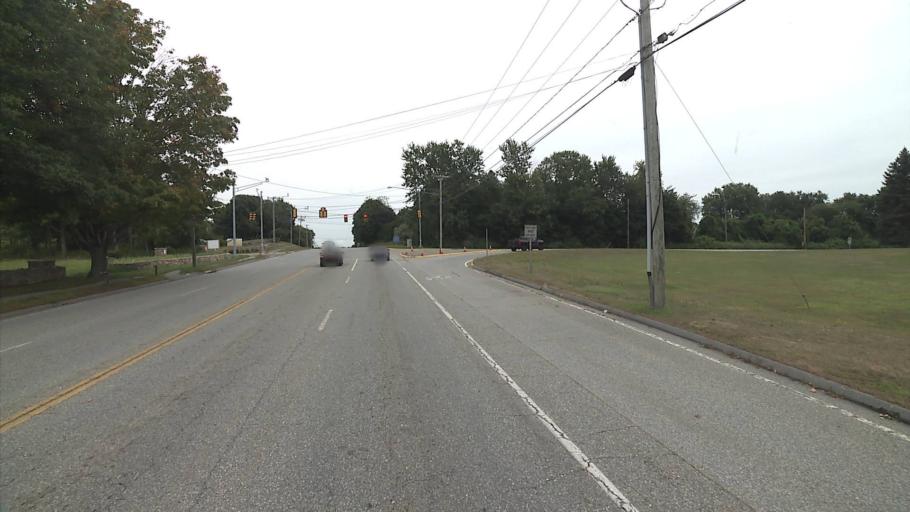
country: US
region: Connecticut
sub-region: New London County
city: Niantic
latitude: 41.3270
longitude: -72.1680
